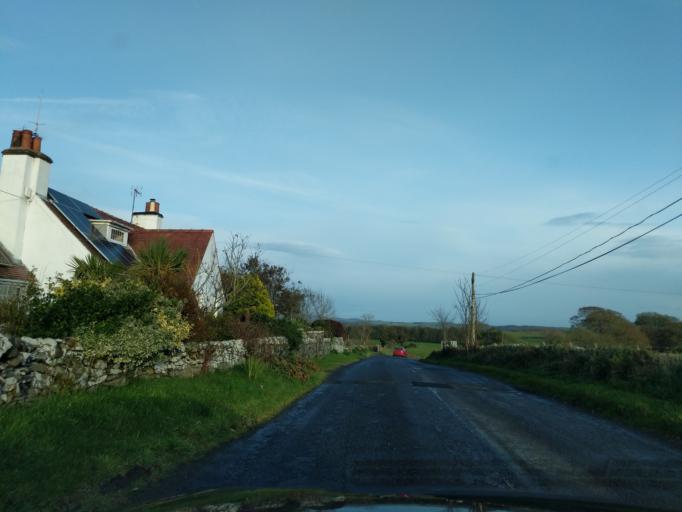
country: GB
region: Scotland
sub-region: Dumfries and Galloway
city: Kirkcudbright
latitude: 54.8111
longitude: -4.1297
